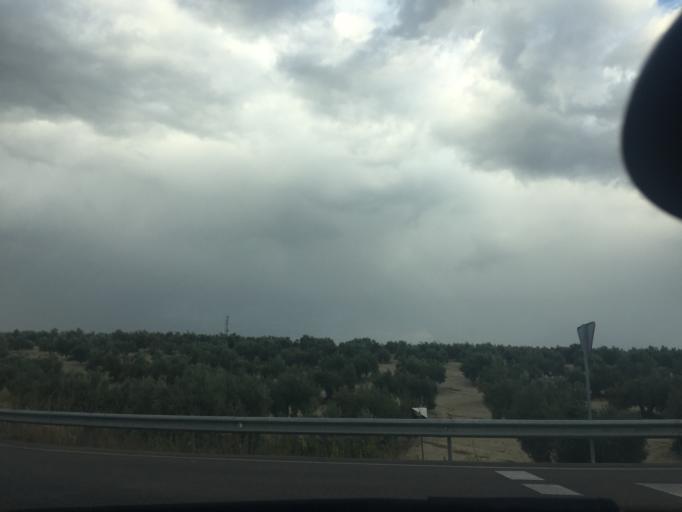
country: ES
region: Andalusia
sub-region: Provincia de Jaen
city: La Guardia de Jaen
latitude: 37.7595
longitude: -3.7368
